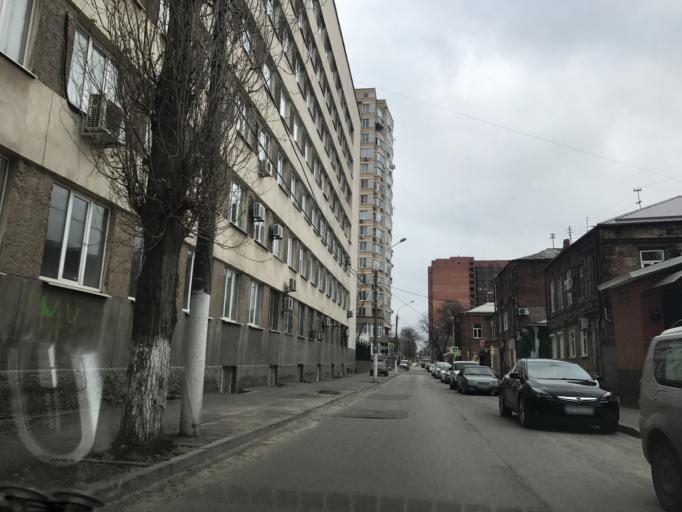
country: RU
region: Rostov
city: Rostov-na-Donu
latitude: 47.2231
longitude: 39.7338
